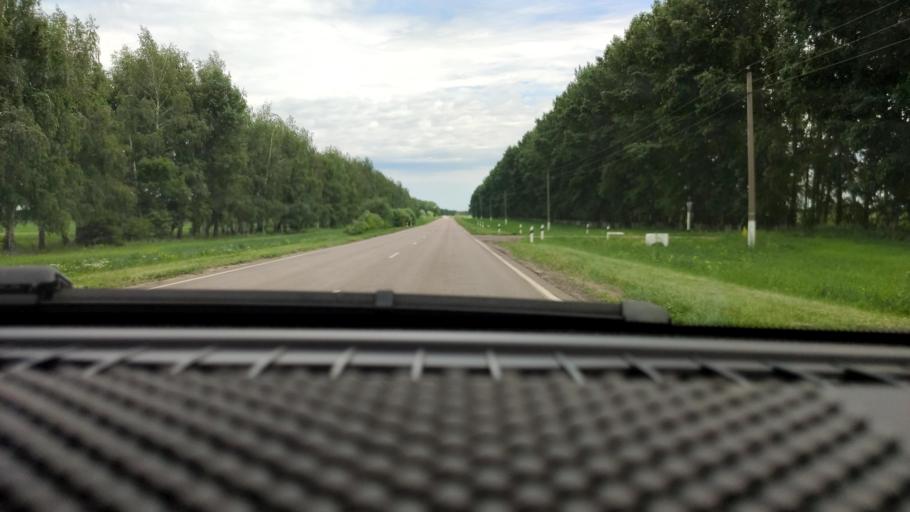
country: RU
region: Voronezj
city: Panino
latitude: 51.6595
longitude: 39.9903
